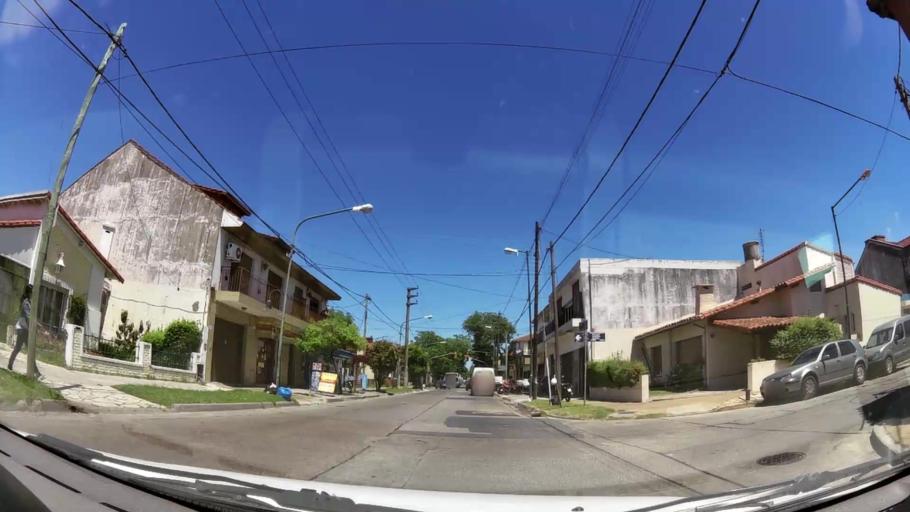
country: AR
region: Buenos Aires
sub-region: Partido de Vicente Lopez
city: Olivos
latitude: -34.5013
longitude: -58.5055
